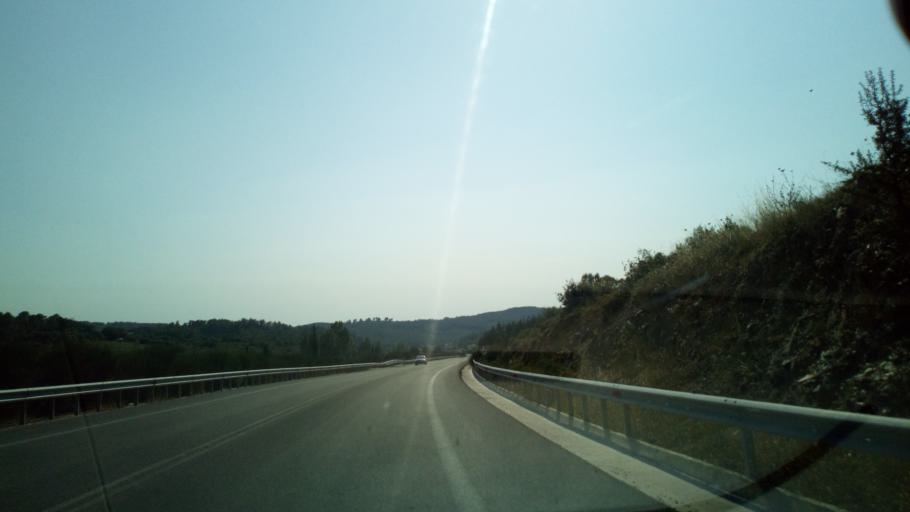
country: GR
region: Central Macedonia
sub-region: Nomos Chalkidikis
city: Polygyros
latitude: 40.3709
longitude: 23.4500
